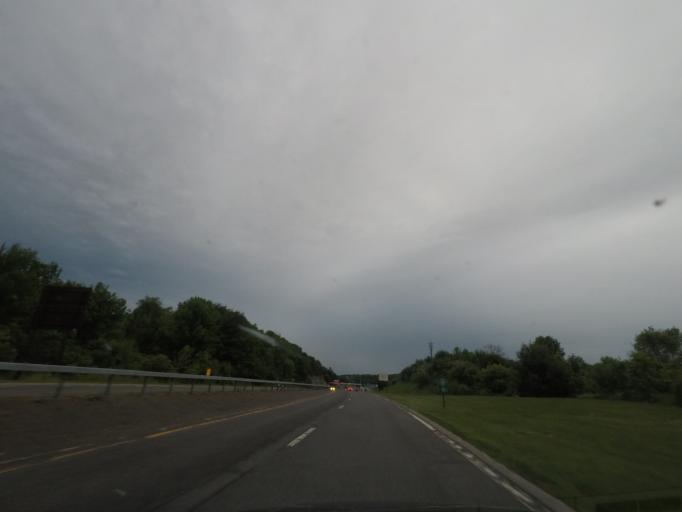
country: US
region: New York
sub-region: Columbia County
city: Chatham
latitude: 42.4151
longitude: -73.5487
